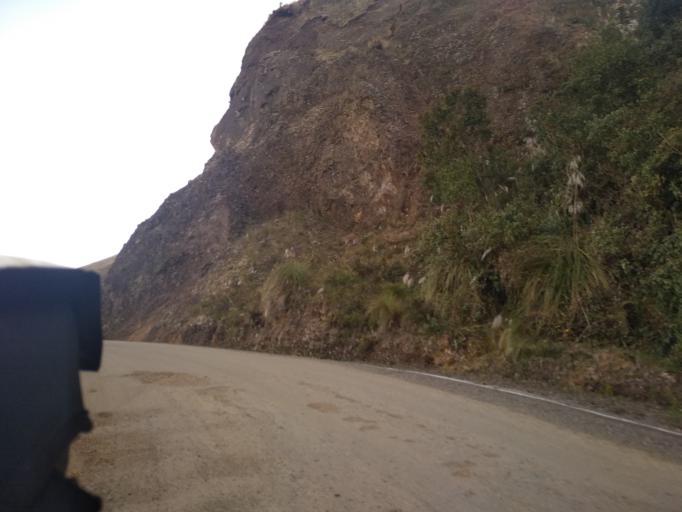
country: PE
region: Amazonas
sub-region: Provincia de Chachapoyas
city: Montevideo
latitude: -6.7220
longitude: -77.8772
